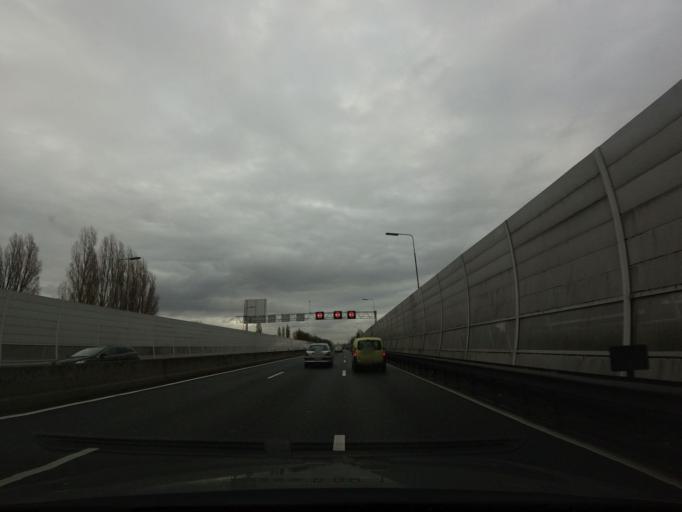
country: NL
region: South Holland
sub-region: Gemeente Schiedam
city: Schiedam
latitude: 51.9427
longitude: 4.4252
